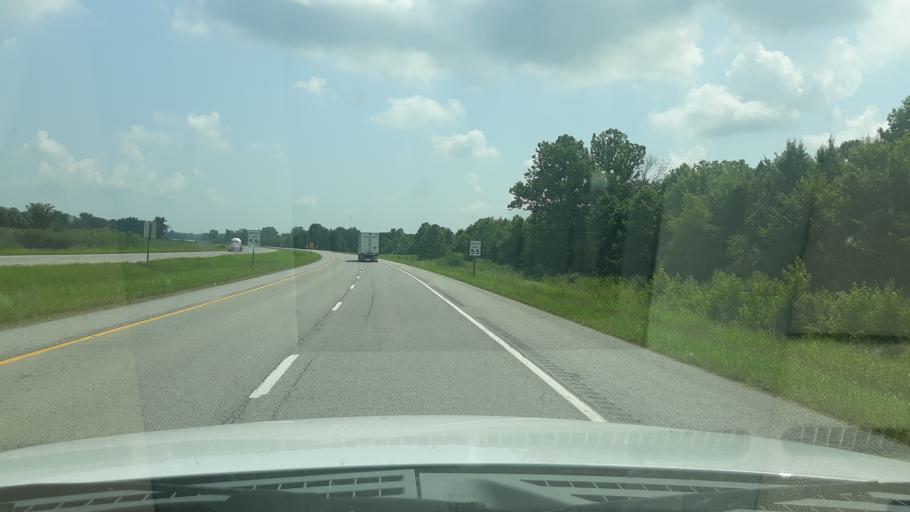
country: US
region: Illinois
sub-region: Saline County
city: Harrisburg
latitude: 37.7323
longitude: -88.5739
